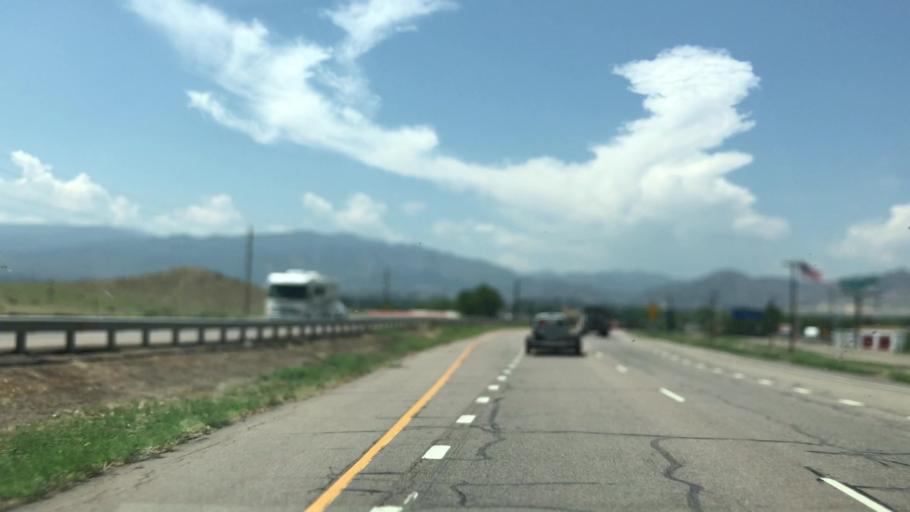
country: US
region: Colorado
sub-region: Fremont County
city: Lincoln Park
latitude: 38.4490
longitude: -105.1745
